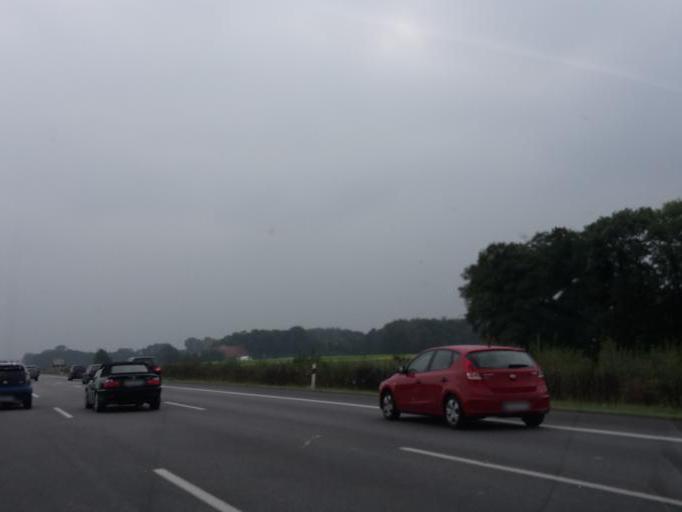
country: DE
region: Lower Saxony
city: Bakum
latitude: 52.7061
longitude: 8.1732
